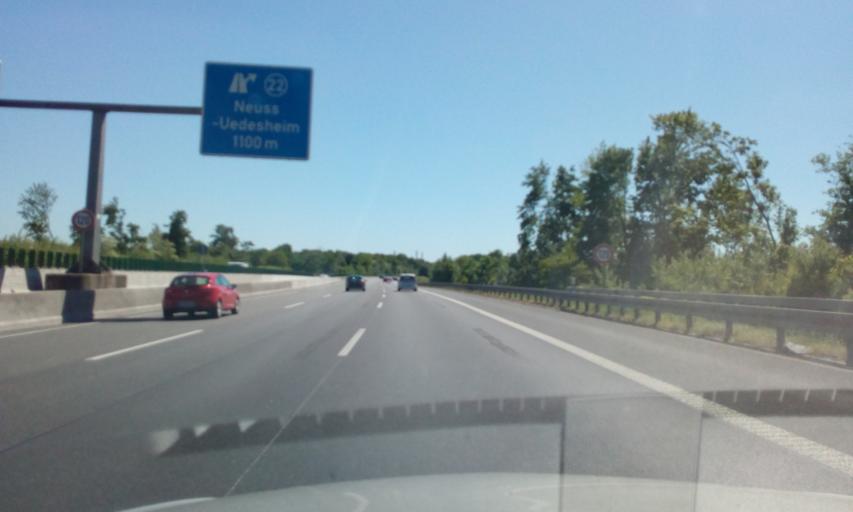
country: DE
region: North Rhine-Westphalia
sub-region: Regierungsbezirk Dusseldorf
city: Dusseldorf
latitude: 51.1767
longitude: 6.7741
